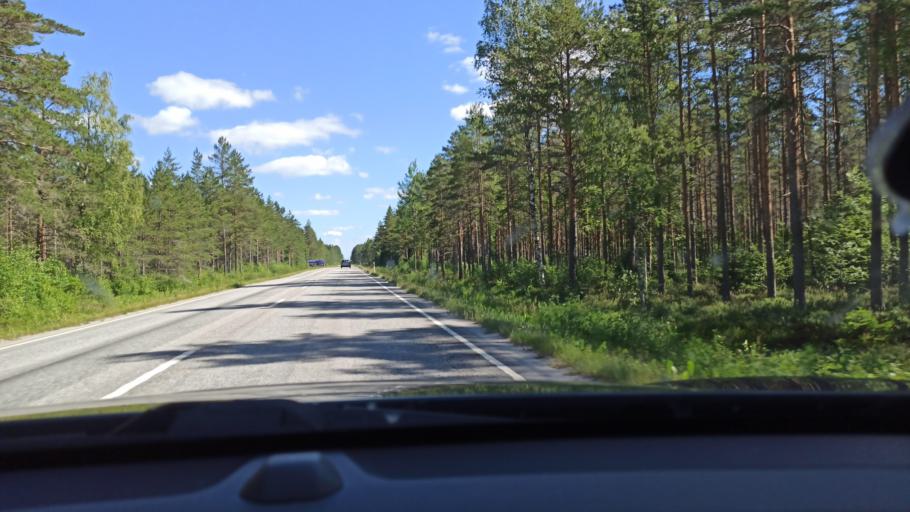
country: FI
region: Ostrobothnia
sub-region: Vaasa
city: Malax
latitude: 62.9760
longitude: 21.6060
